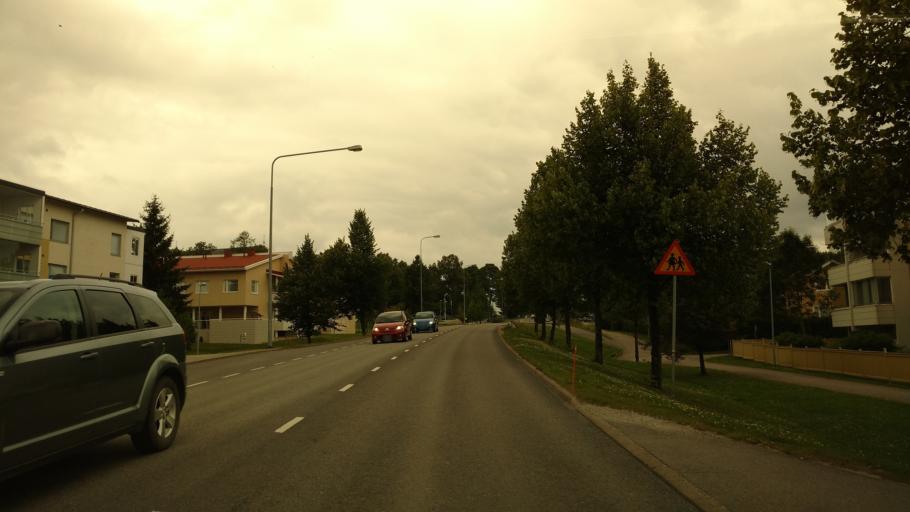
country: FI
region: Varsinais-Suomi
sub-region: Salo
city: Halikko
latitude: 60.3984
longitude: 23.0762
